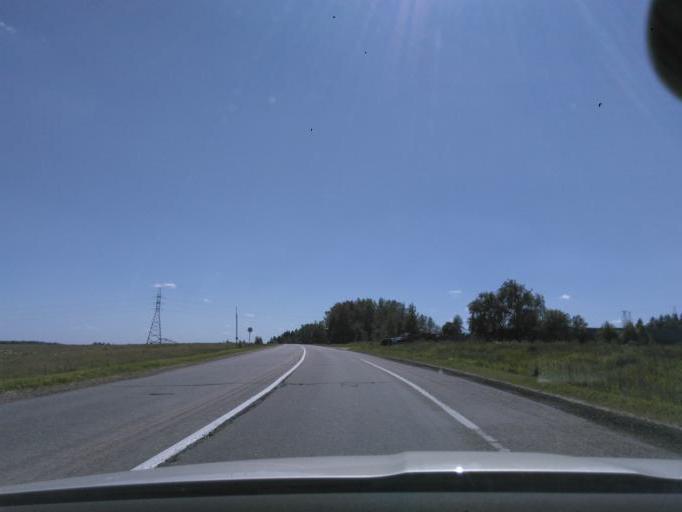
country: RU
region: Moskovskaya
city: Solnechnogorsk
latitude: 56.1651
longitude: 36.9260
